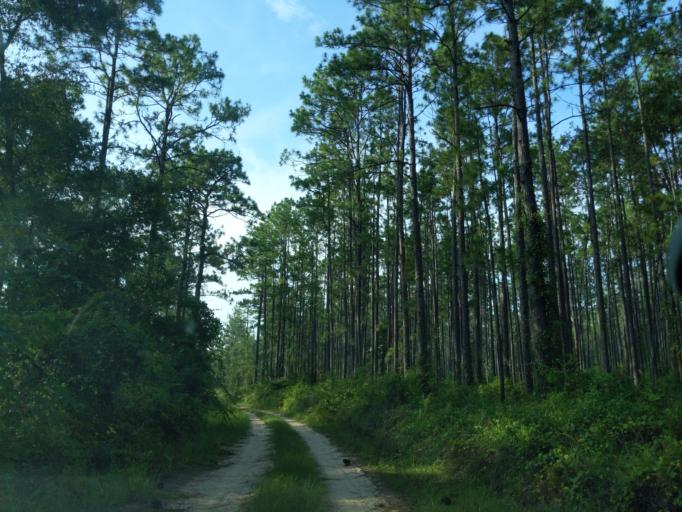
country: US
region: Florida
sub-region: Leon County
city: Tallahassee
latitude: 30.3529
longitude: -84.3608
